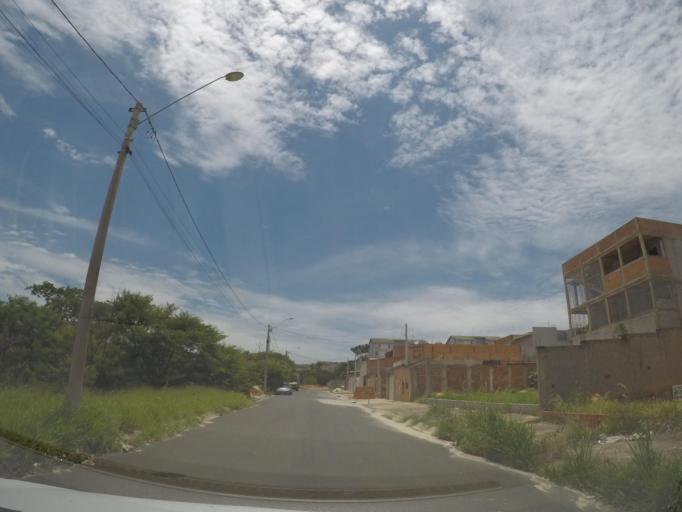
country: BR
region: Sao Paulo
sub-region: Hortolandia
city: Hortolandia
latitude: -22.8427
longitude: -47.2003
